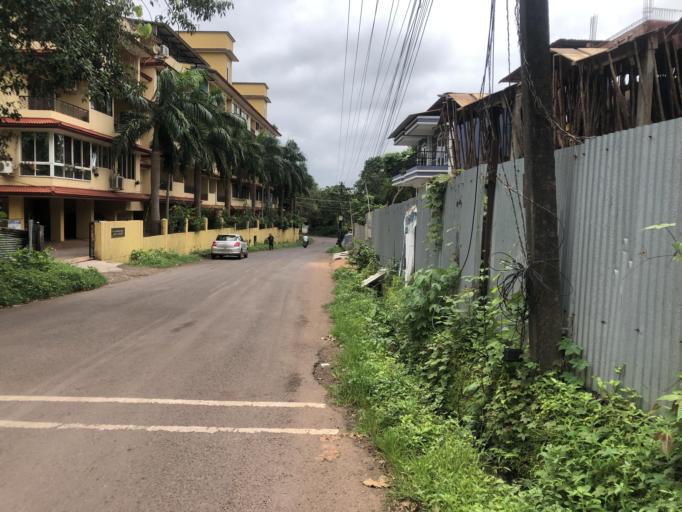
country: IN
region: Goa
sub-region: North Goa
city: Serula
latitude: 15.5458
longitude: 73.8293
